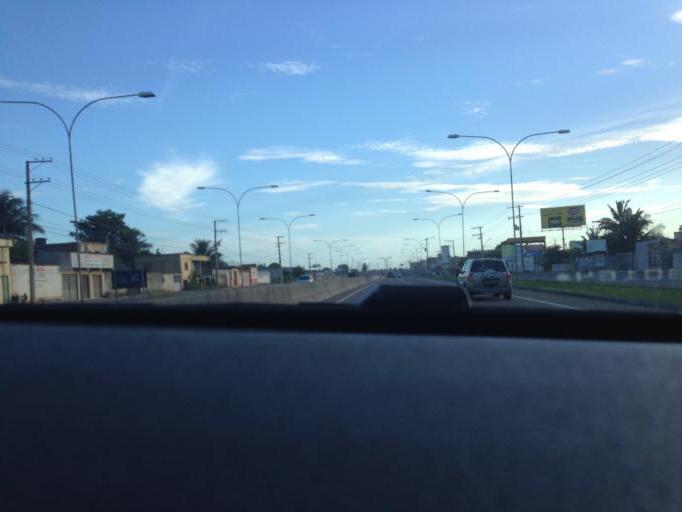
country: BR
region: Espirito Santo
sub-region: Vila Velha
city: Vila Velha
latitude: -20.4428
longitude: -40.3331
